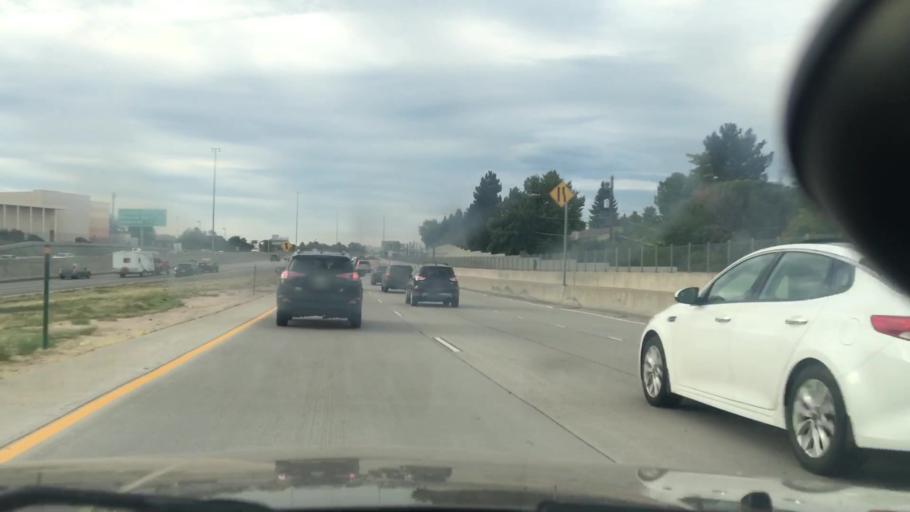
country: US
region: Colorado
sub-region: Arapahoe County
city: Cherry Hills Village
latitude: 39.6522
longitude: -104.9185
